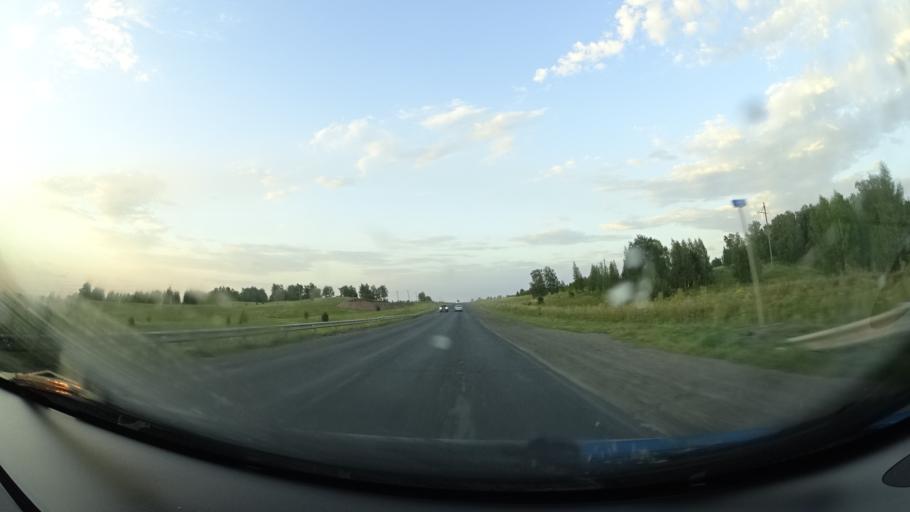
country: RU
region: Orenburg
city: Severnoye
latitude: 54.1835
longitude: 52.6630
